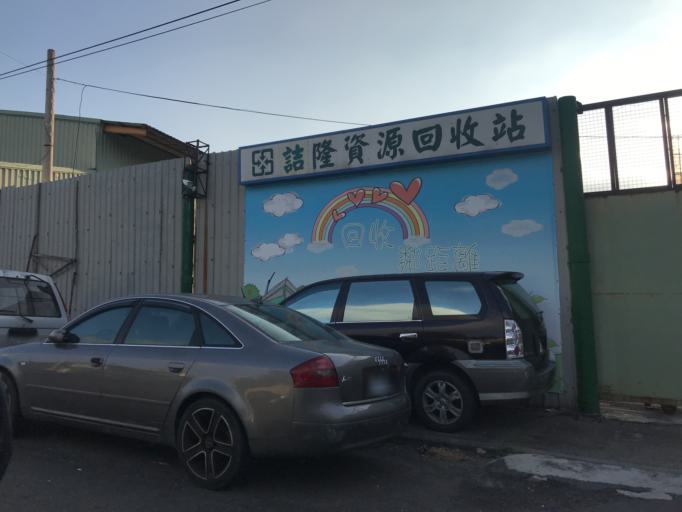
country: TW
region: Taiwan
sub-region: Taichung City
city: Taichung
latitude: 24.1216
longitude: 120.6926
